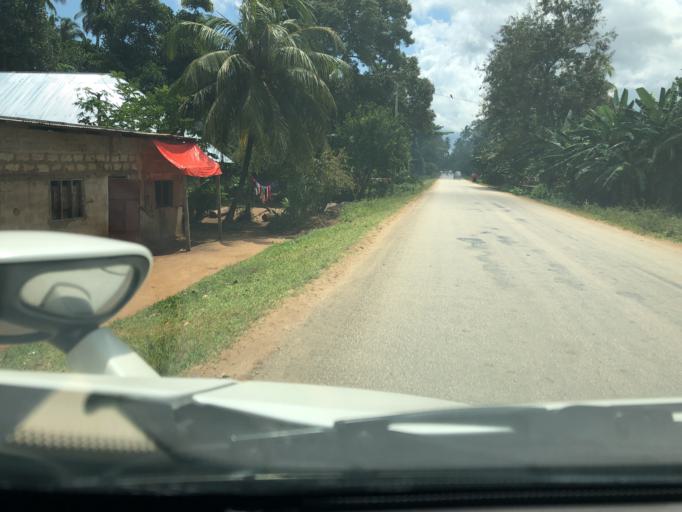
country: TZ
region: Zanzibar Central/South
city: Koani
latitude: -6.0848
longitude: 39.2521
